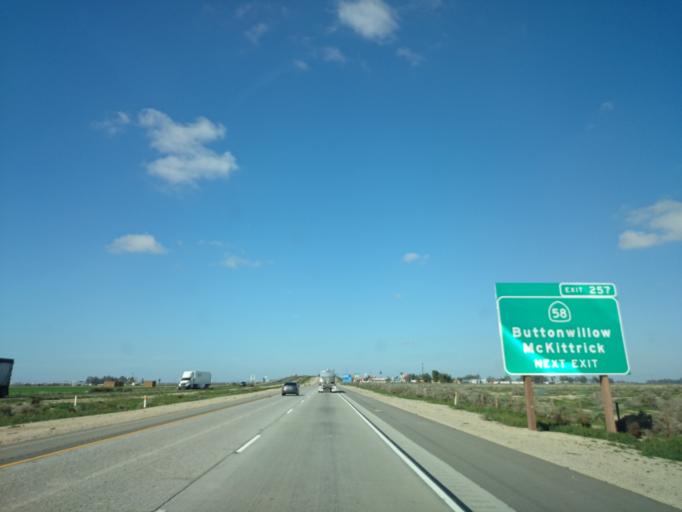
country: US
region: California
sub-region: Kern County
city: Buttonwillow
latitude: 35.3933
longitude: -119.3895
